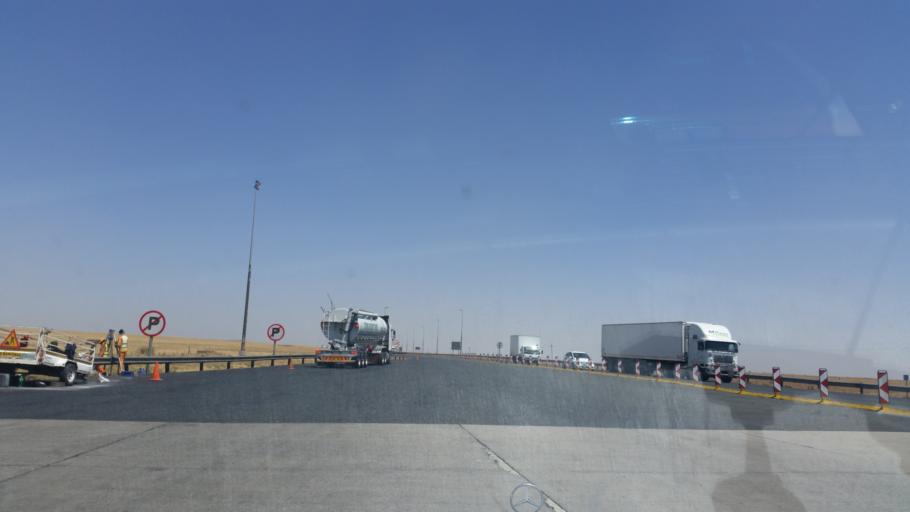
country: ZA
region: Orange Free State
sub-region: Lejweleputswa District Municipality
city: Brandfort
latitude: -28.7993
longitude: 26.6900
